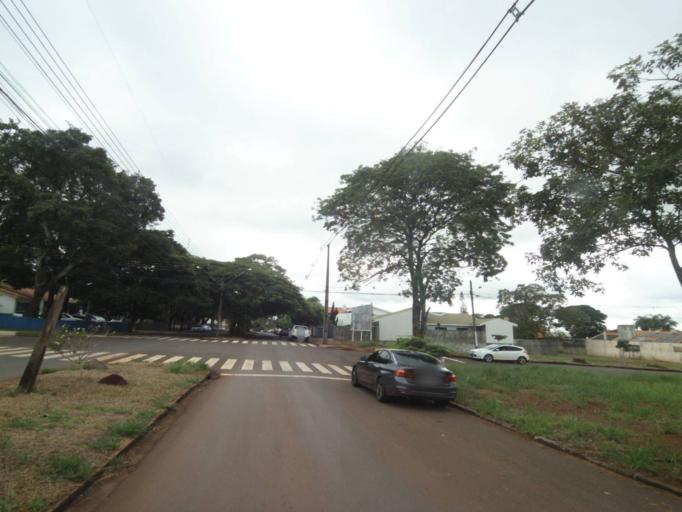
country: BR
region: Parana
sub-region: Campo Mourao
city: Campo Mourao
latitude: -24.0434
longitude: -52.3694
